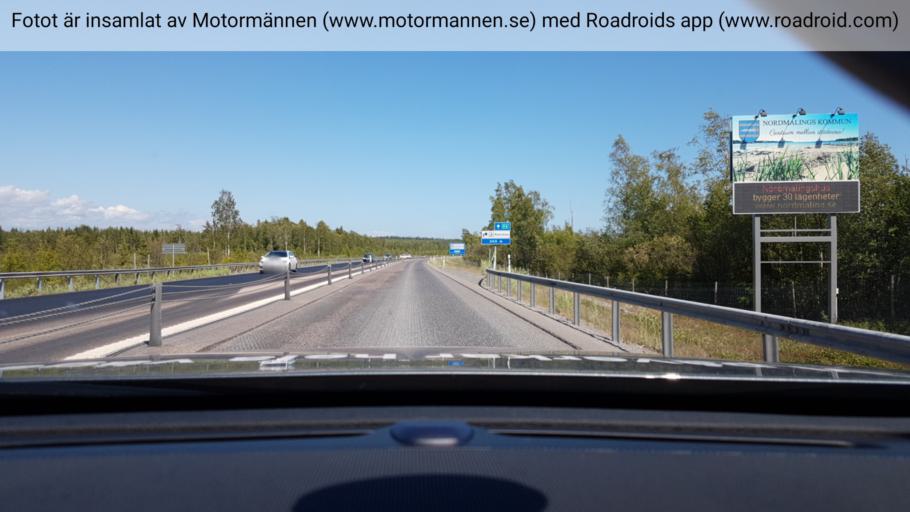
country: SE
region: Vaesterbotten
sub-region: Nordmalings Kommun
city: Nordmaling
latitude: 63.5685
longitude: 19.4343
